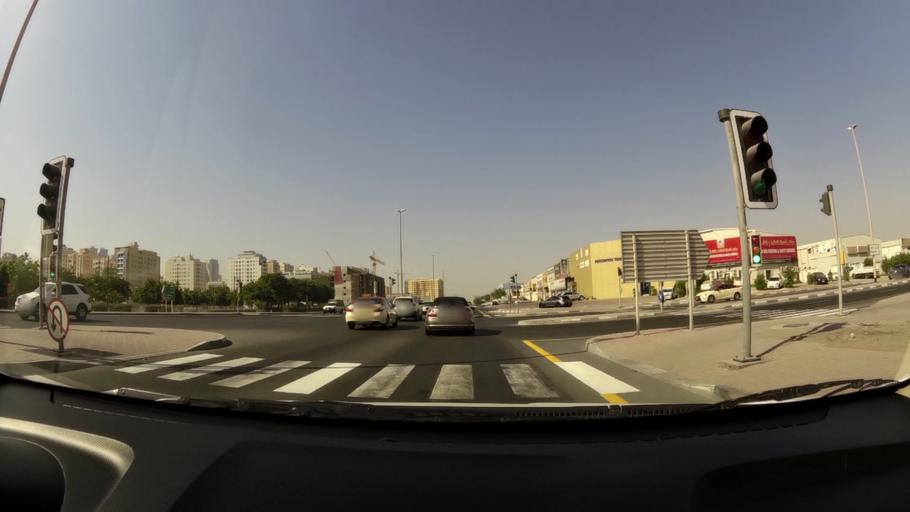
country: AE
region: Ash Shariqah
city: Sharjah
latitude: 25.2884
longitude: 55.3838
